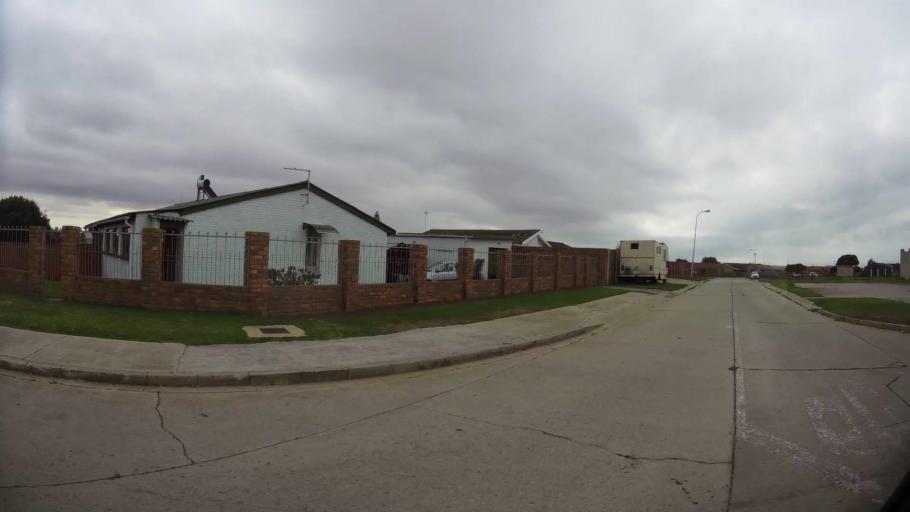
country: ZA
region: Eastern Cape
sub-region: Nelson Mandela Bay Metropolitan Municipality
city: Port Elizabeth
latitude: -33.9157
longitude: 25.5719
